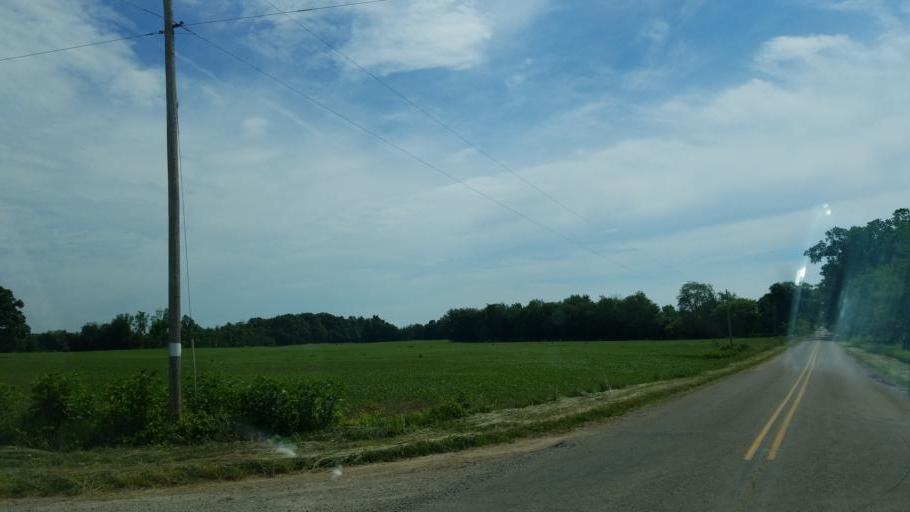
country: US
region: Michigan
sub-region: Barry County
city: Nashville
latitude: 42.6834
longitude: -85.0148
